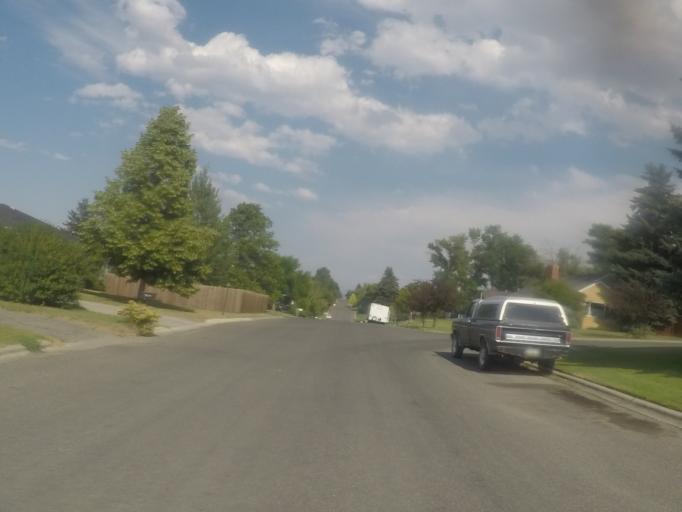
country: US
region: Montana
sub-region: Lewis and Clark County
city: Helena
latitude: 46.5831
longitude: -112.0194
